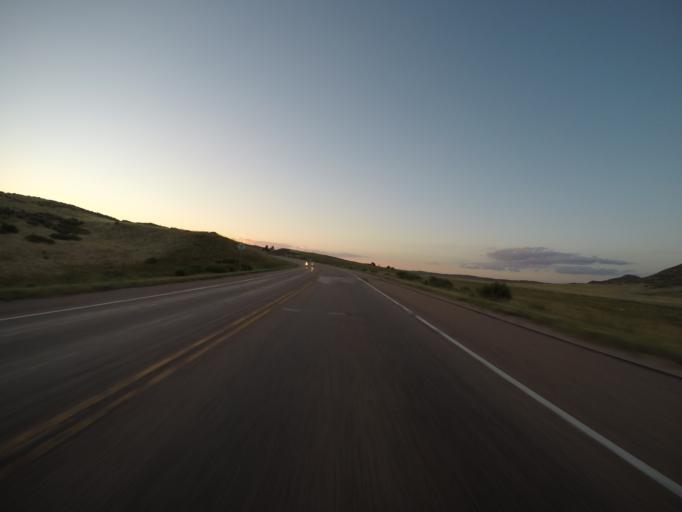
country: US
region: Colorado
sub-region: Larimer County
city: Laporte
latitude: 40.7556
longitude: -105.1710
